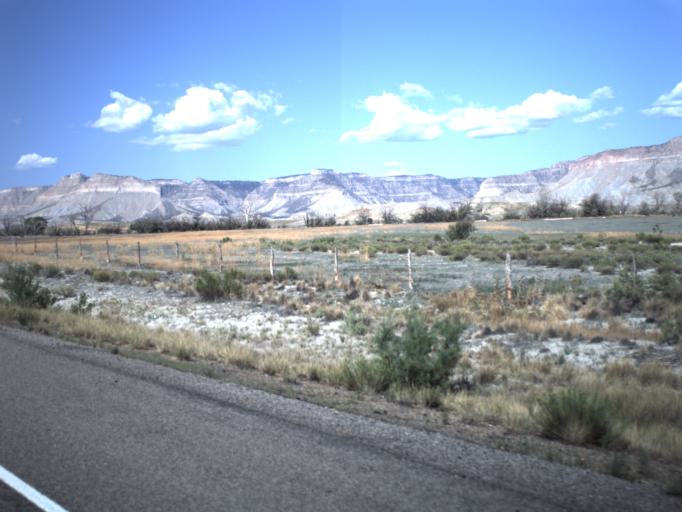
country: US
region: Utah
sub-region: Emery County
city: Castle Dale
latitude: 39.1706
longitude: -111.0558
